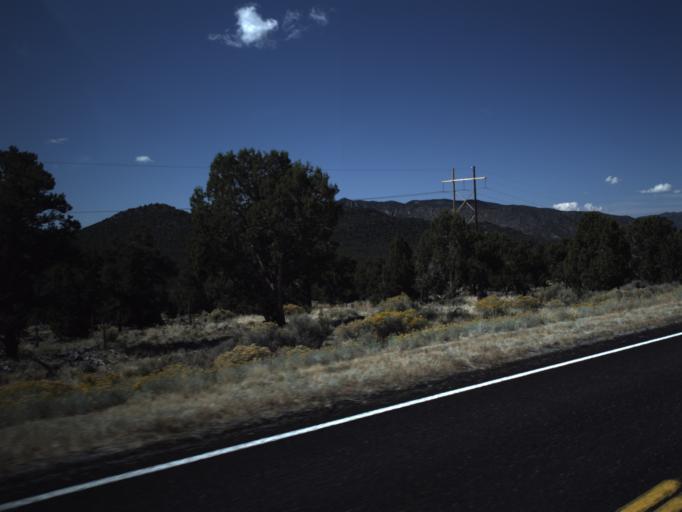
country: US
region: Utah
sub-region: Washington County
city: Enterprise
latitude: 37.6113
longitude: -113.3982
